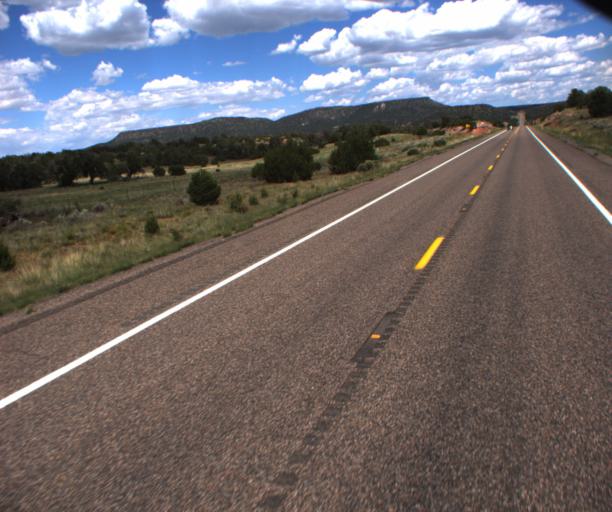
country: US
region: Arizona
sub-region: Apache County
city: Springerville
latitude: 34.1603
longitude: -109.0896
